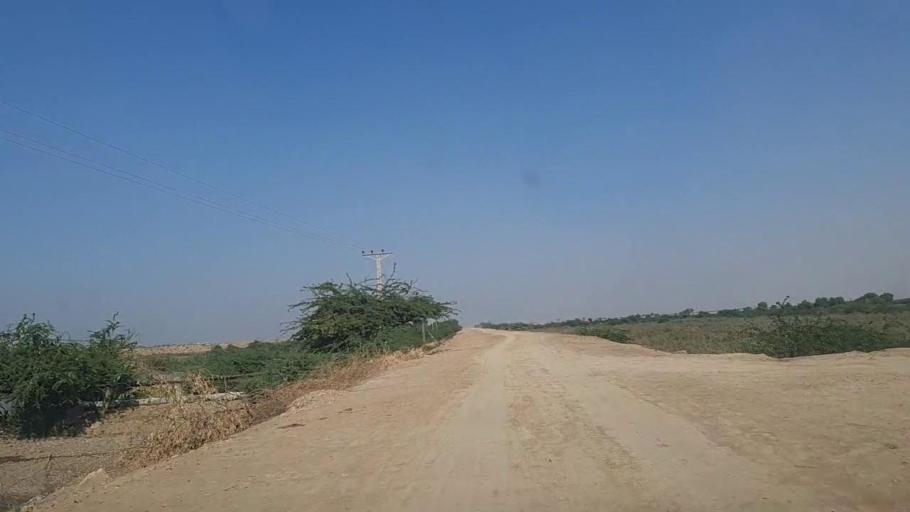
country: PK
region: Sindh
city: Daro Mehar
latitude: 24.9027
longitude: 68.0745
